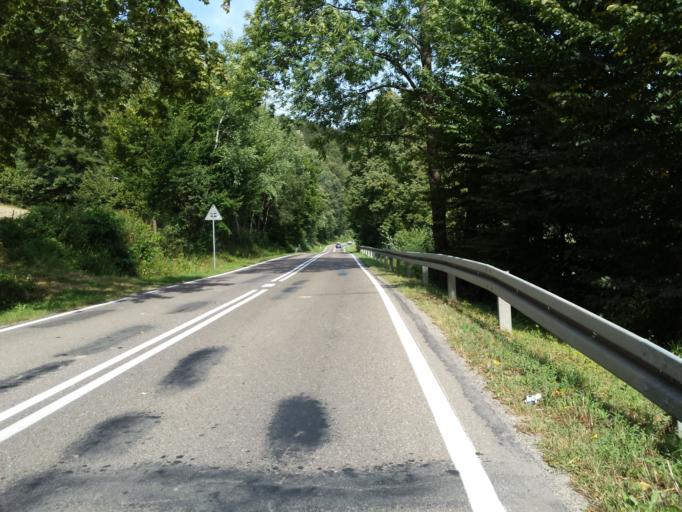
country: PL
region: Subcarpathian Voivodeship
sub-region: Powiat leski
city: Baligrod
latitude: 49.3655
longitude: 22.2735
